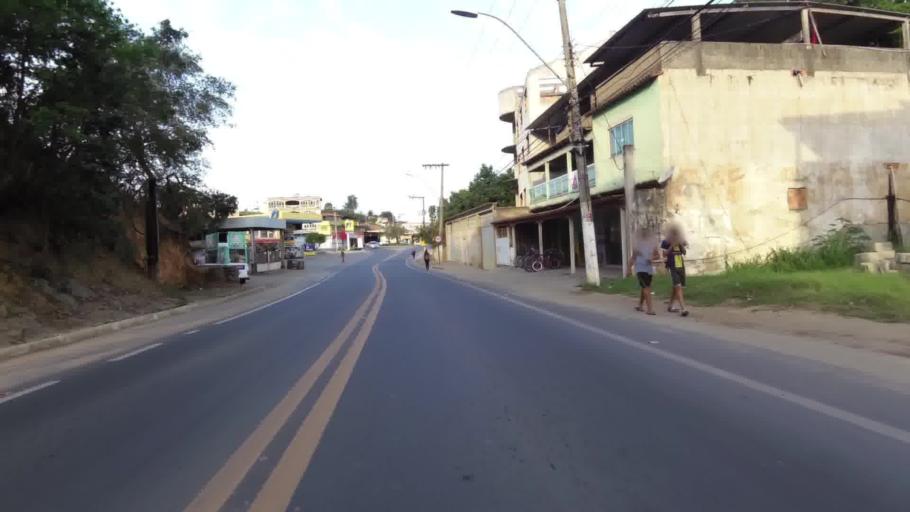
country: BR
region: Espirito Santo
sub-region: Piuma
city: Piuma
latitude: -20.8348
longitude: -40.7242
